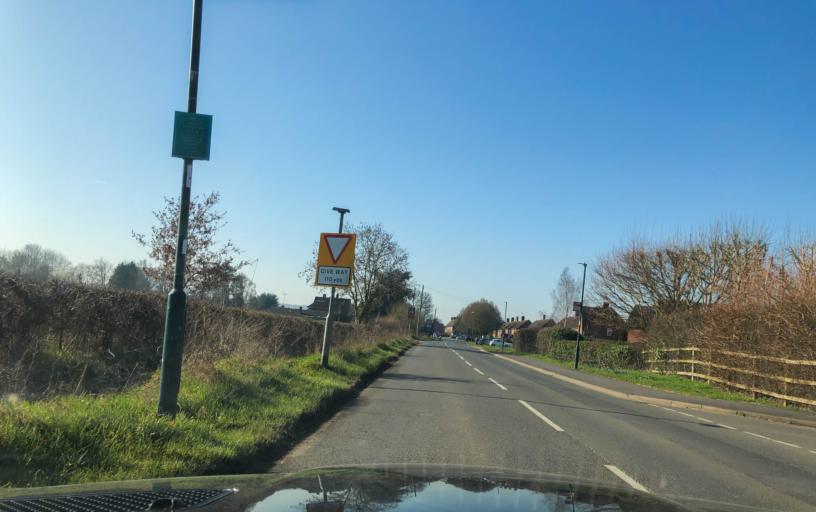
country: GB
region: England
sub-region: Warwickshire
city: Wellesbourne Mountford
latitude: 52.1999
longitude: -1.5873
